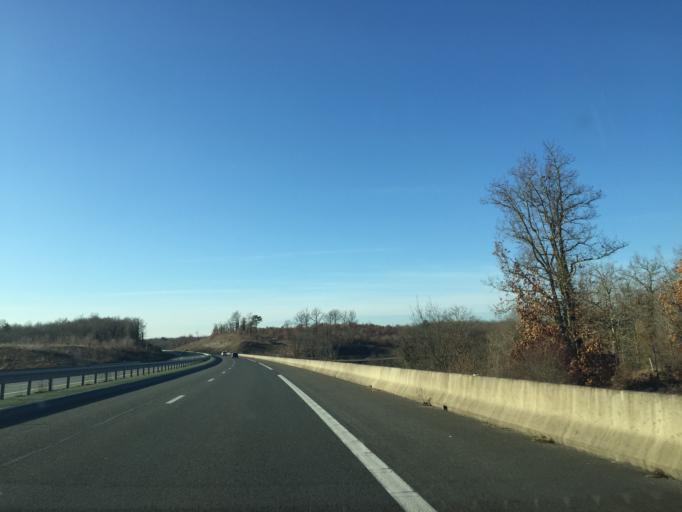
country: FR
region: Aquitaine
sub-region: Departement de la Dordogne
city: Thenon
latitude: 45.1756
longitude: 1.0160
